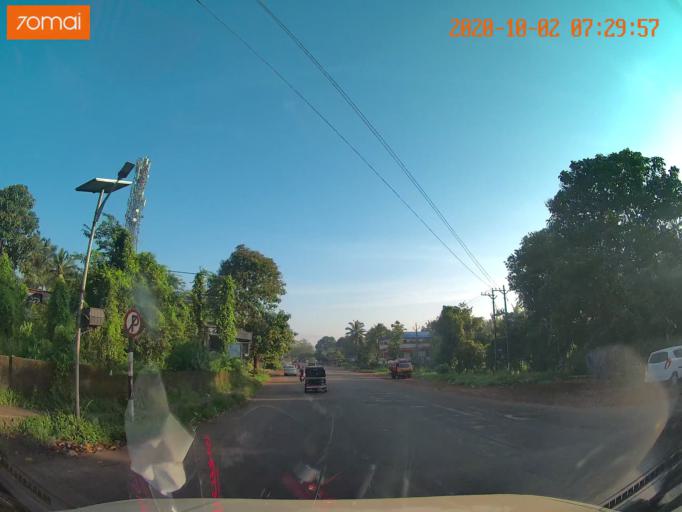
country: IN
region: Kerala
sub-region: Malappuram
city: Pariyapuram
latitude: 11.0370
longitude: 75.9375
